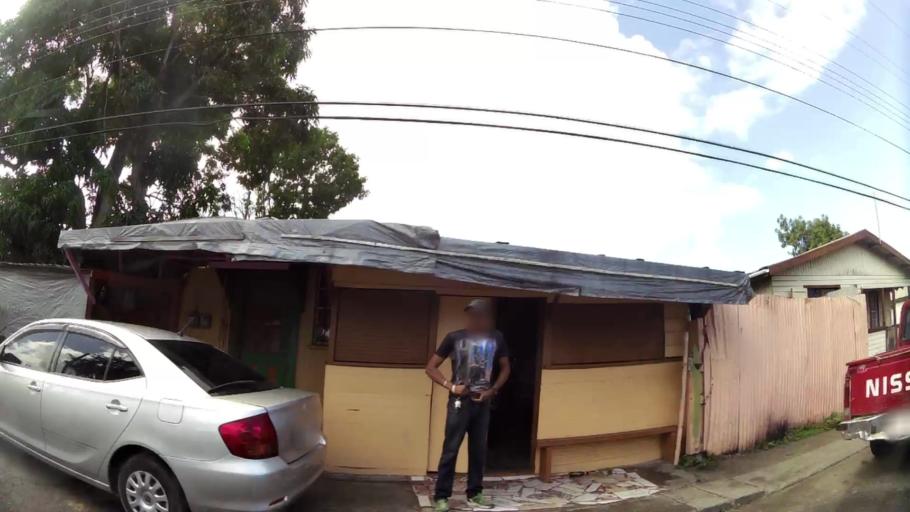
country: AG
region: Saint John
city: Saint John's
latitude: 17.1124
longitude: -61.8446
